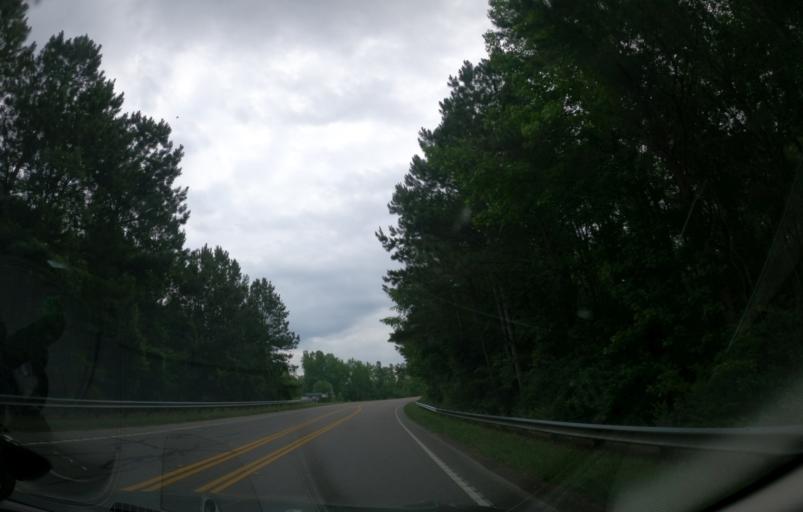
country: US
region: South Carolina
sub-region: Aiken County
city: Aiken
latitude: 33.5772
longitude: -81.6027
